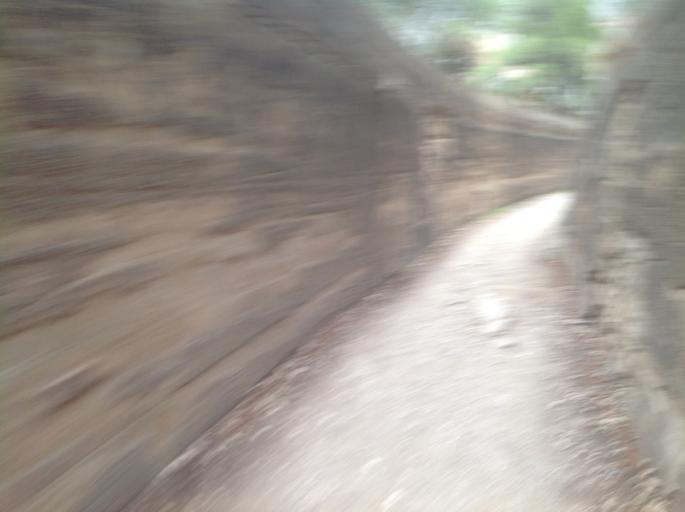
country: ES
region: Andalusia
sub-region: Provincia de Malaga
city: Carratraca
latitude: 36.9179
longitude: -4.7770
